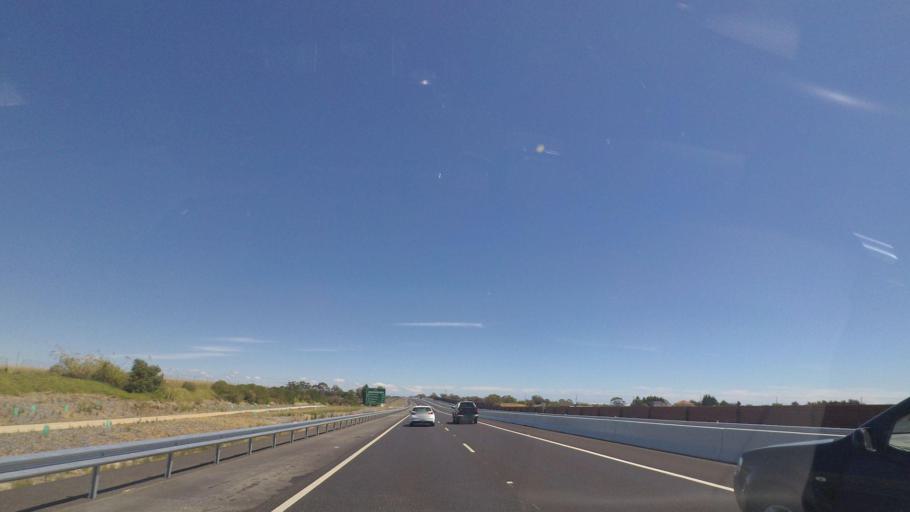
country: AU
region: Victoria
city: Heatherton
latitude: -37.9659
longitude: 145.1171
